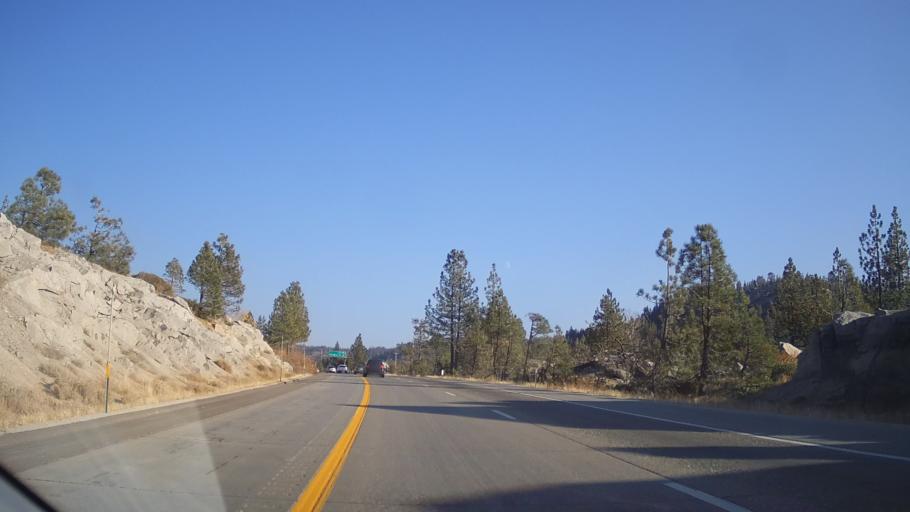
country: US
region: California
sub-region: Nevada County
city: Truckee
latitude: 39.3123
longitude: -120.5069
